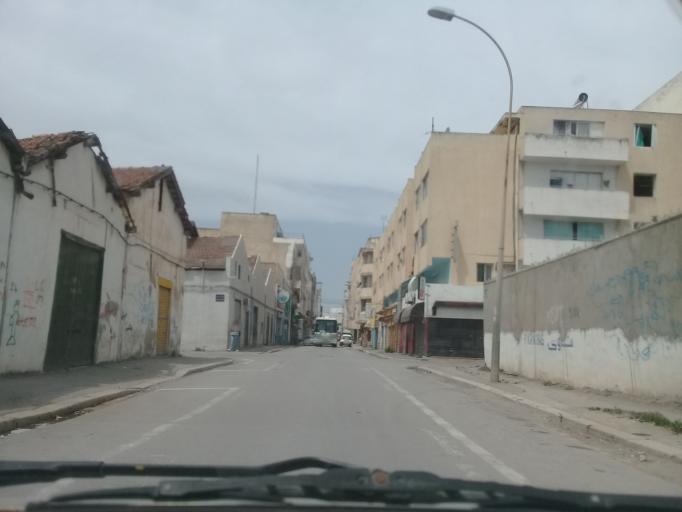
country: TN
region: Tunis
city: Tunis
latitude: 36.7954
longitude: 10.1853
